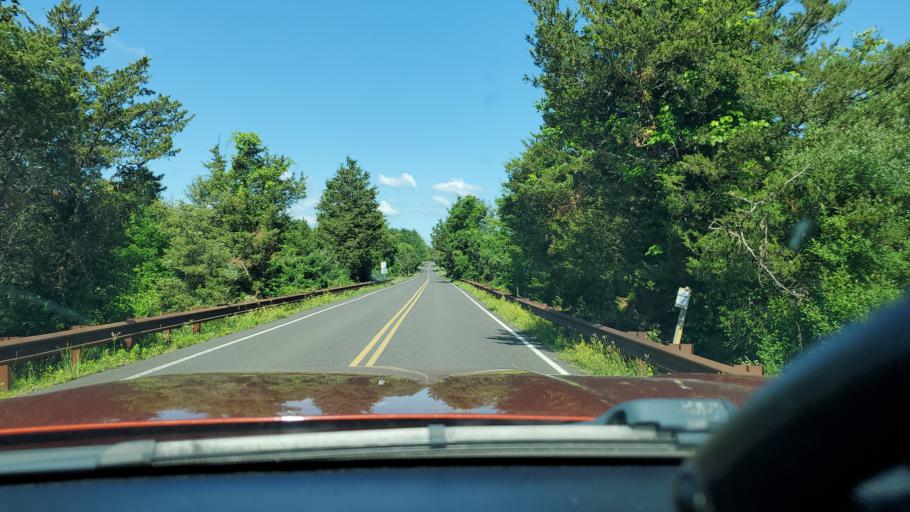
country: US
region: Pennsylvania
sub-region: Montgomery County
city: Red Hill
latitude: 40.3543
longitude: -75.4883
